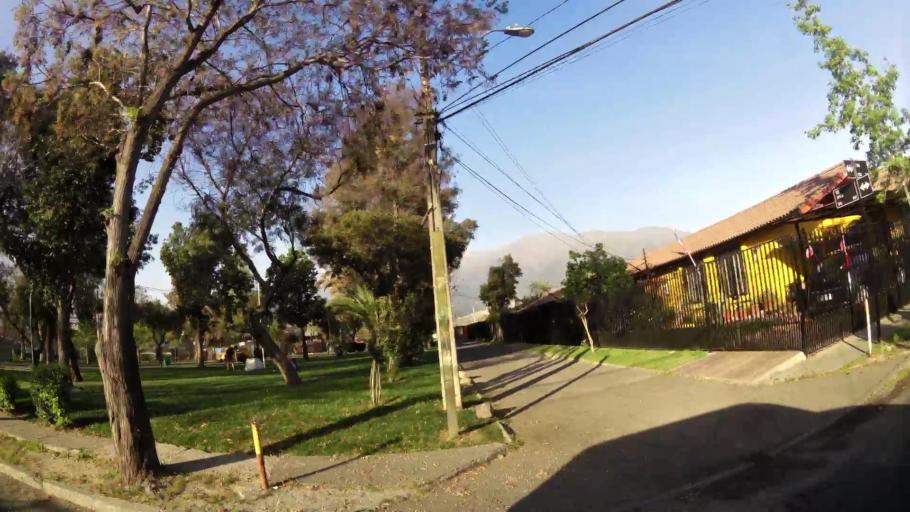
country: CL
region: Santiago Metropolitan
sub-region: Provincia de Santiago
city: La Pintana
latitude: -33.5440
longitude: -70.5792
